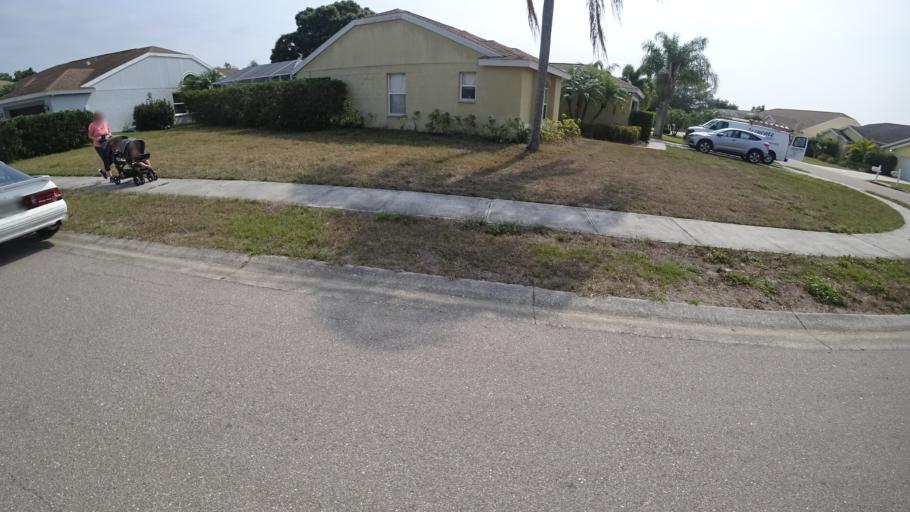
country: US
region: Florida
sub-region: Manatee County
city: Samoset
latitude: 27.4599
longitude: -82.5131
